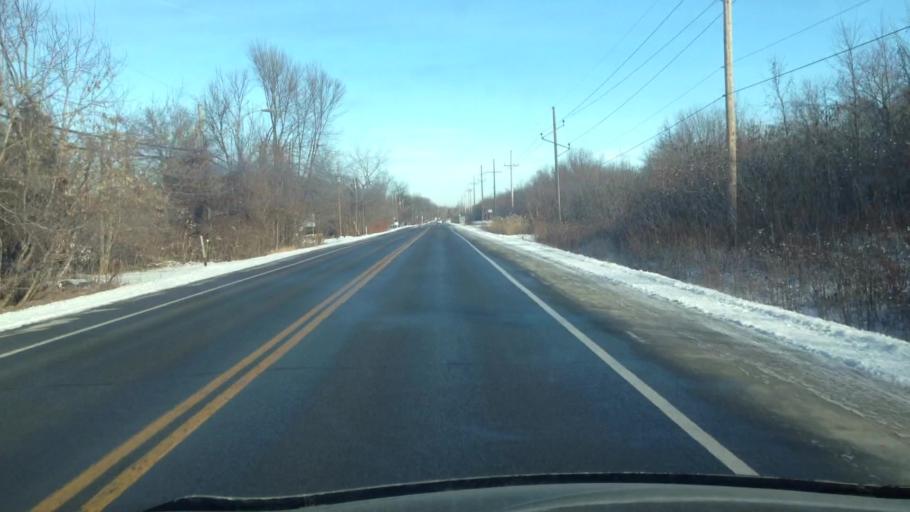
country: CA
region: Quebec
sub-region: Monteregie
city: Beauharnois
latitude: 45.3376
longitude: -73.8133
